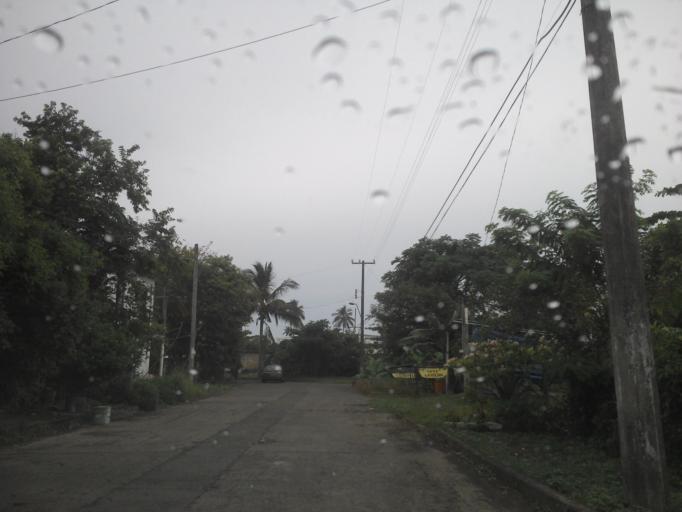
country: MX
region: Veracruz
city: Nautla
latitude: 20.2114
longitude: -96.7781
